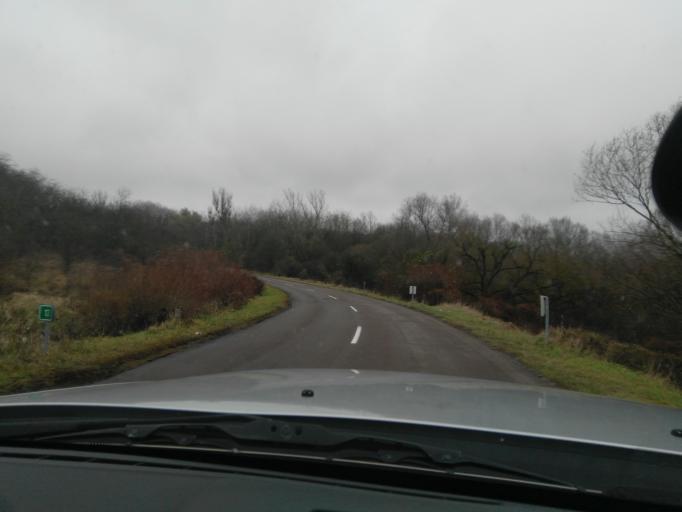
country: HU
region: Nograd
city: Kazar
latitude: 48.0465
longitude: 19.9021
